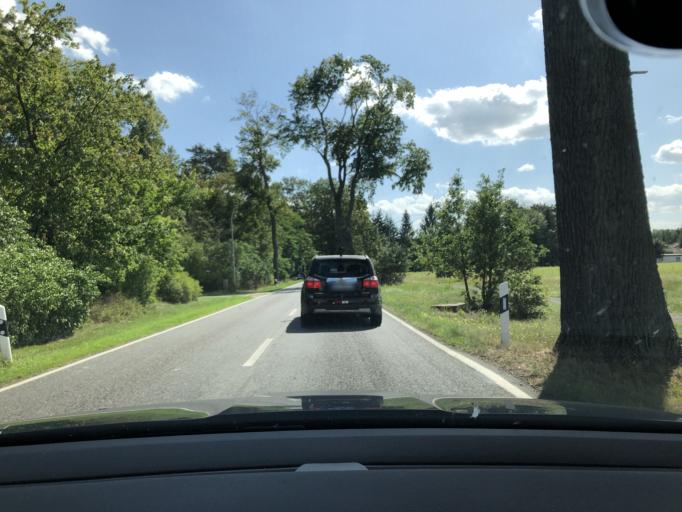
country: DE
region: Brandenburg
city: Ruthnick
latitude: 52.8787
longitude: 13.0033
